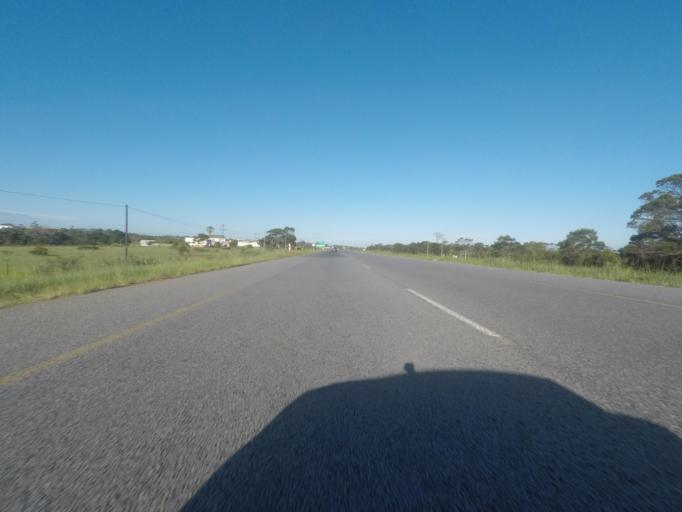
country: ZA
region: Eastern Cape
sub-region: Buffalo City Metropolitan Municipality
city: East London
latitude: -33.0546
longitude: 27.8037
